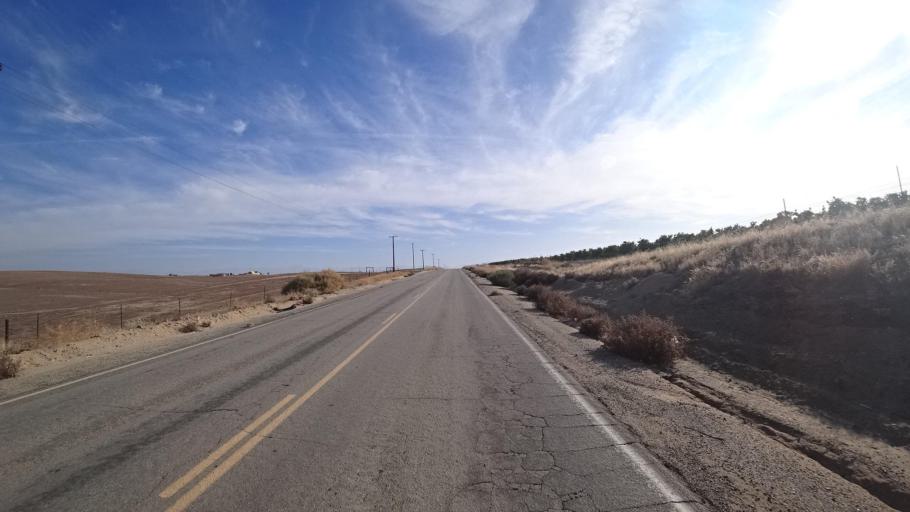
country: US
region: California
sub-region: Kern County
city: McFarland
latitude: 35.6025
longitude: -119.0799
